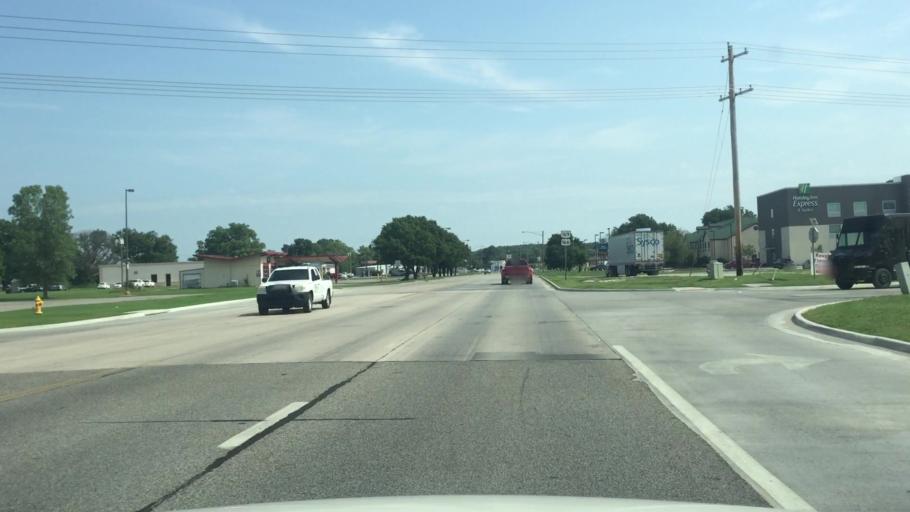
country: US
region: Kansas
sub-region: Montgomery County
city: Coffeyville
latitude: 37.0357
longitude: -95.6002
